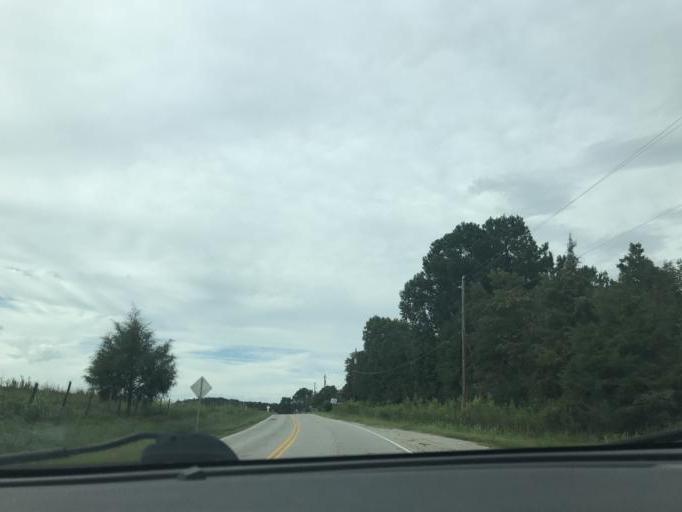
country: US
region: South Carolina
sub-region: Cherokee County
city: East Gaffney
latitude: 35.1116
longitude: -81.6503
